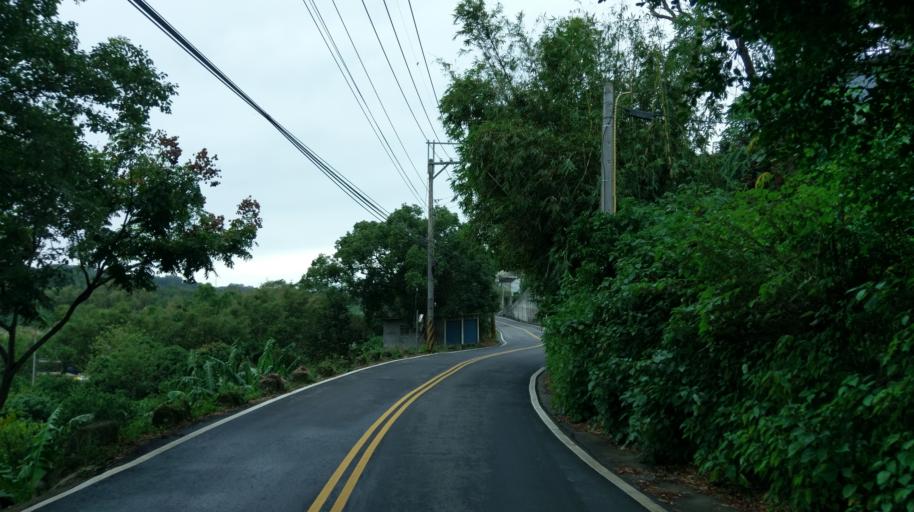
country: TW
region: Taiwan
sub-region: Hsinchu
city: Hsinchu
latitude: 24.7300
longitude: 120.9601
